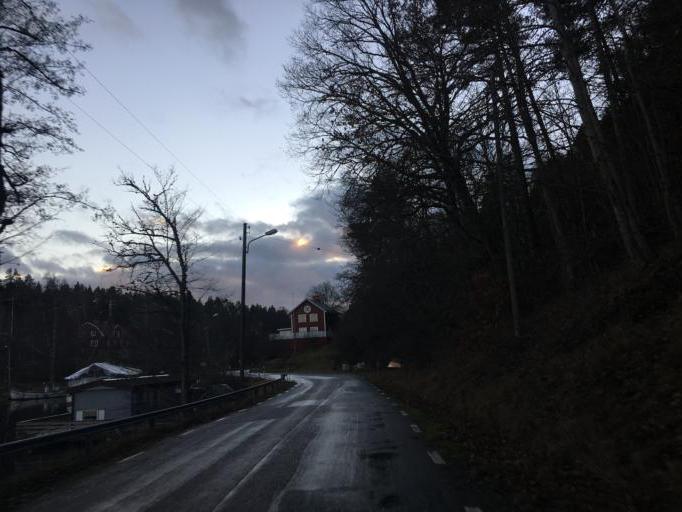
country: SE
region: Kalmar
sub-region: Vasterviks Kommun
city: Vaestervik
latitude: 57.5780
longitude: 16.5135
